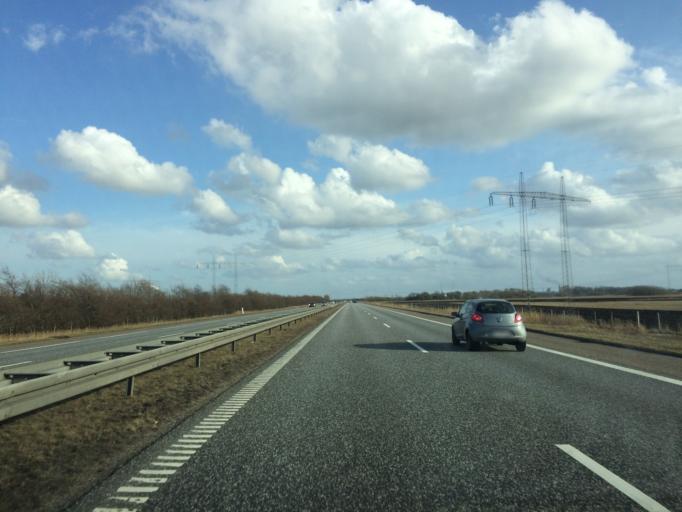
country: DK
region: North Denmark
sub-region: Alborg Kommune
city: Vestbjerg
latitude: 57.1127
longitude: 9.9508
